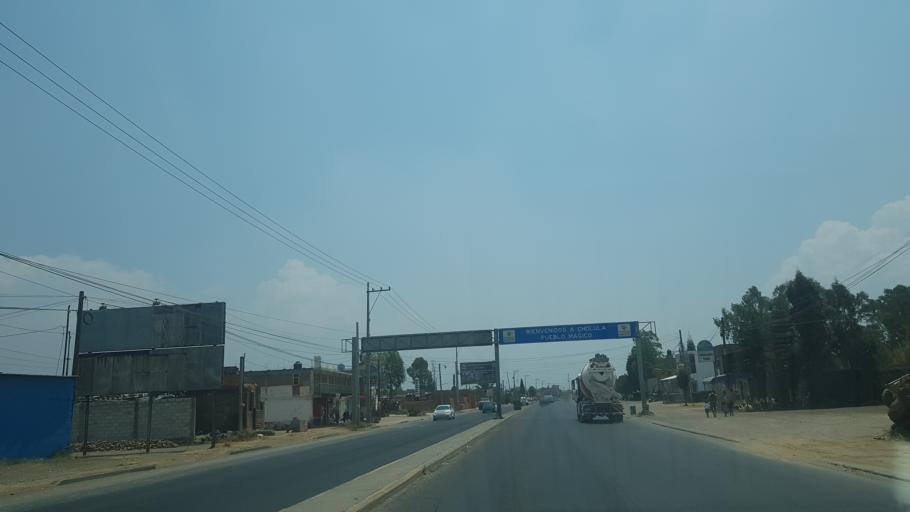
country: MX
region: Puebla
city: Cholula
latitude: 19.0770
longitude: -98.3230
